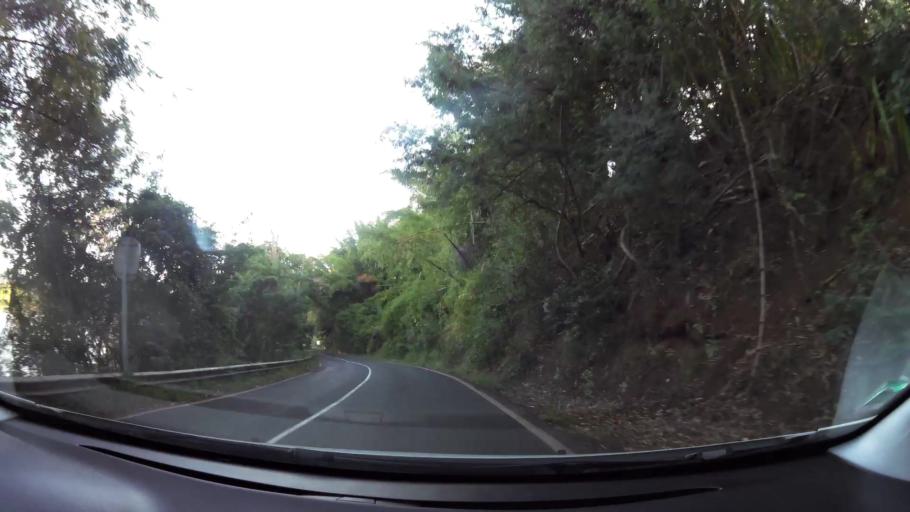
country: YT
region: Dembeni
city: Dembeni
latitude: -12.8223
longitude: 45.1960
